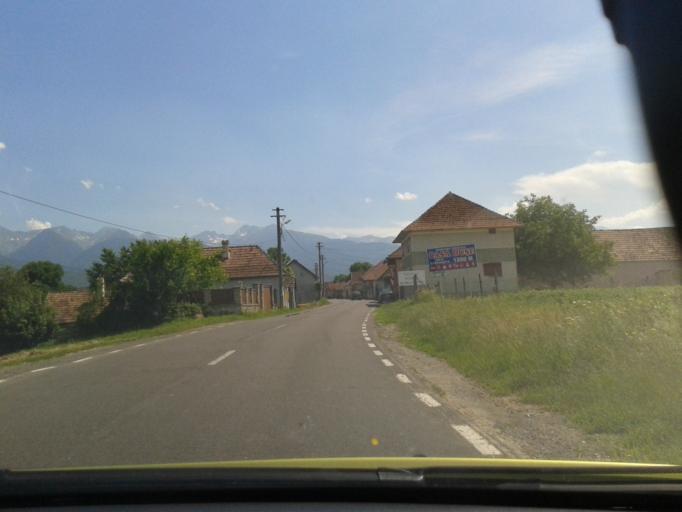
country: RO
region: Sibiu
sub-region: Comuna Cartisoara
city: Cartisoara
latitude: 45.7322
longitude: 24.5747
